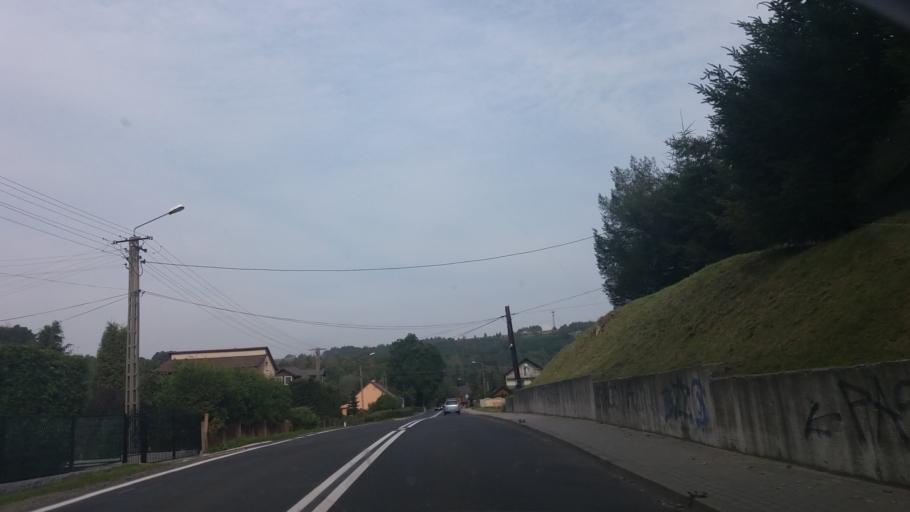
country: PL
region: Lesser Poland Voivodeship
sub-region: Powiat chrzanowski
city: Babice
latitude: 50.0797
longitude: 19.4391
